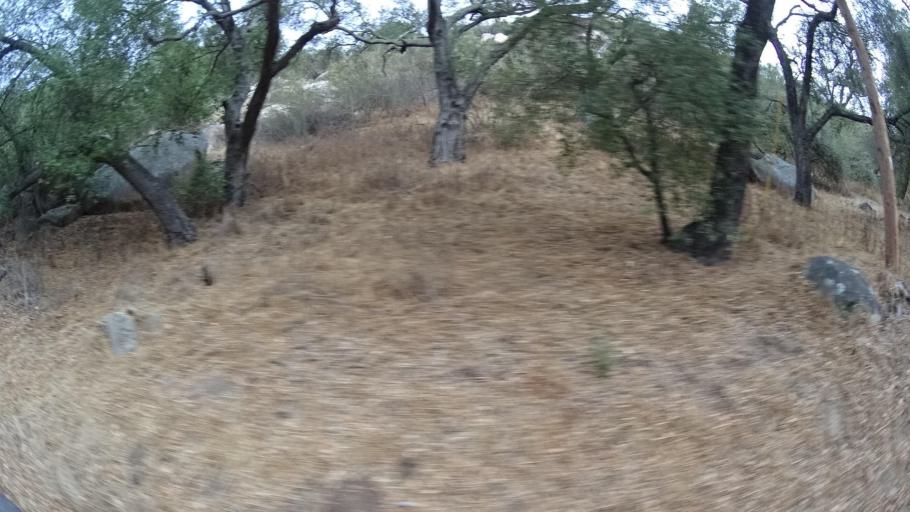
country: US
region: California
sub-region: San Diego County
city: San Pasqual
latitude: 33.0511
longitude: -116.9703
